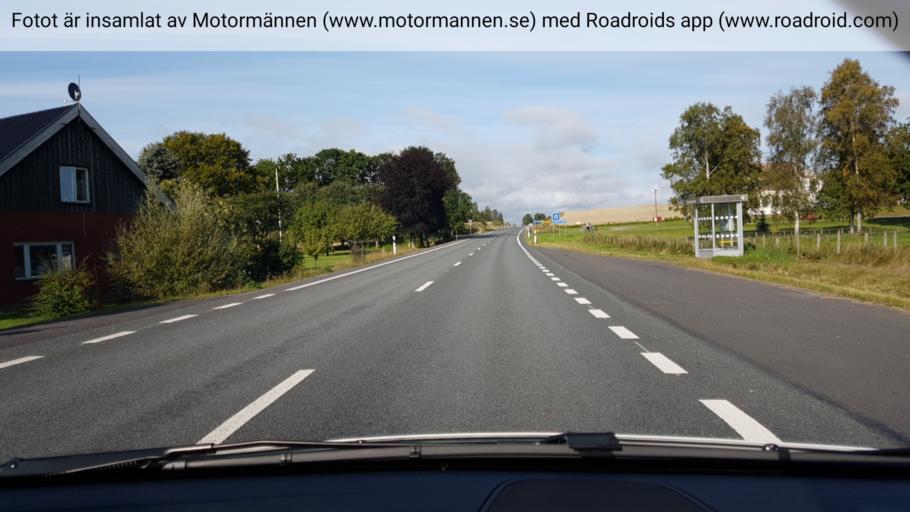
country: SE
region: Vaestra Goetaland
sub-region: Falkopings Kommun
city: Akarp
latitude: 58.1240
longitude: 13.7336
